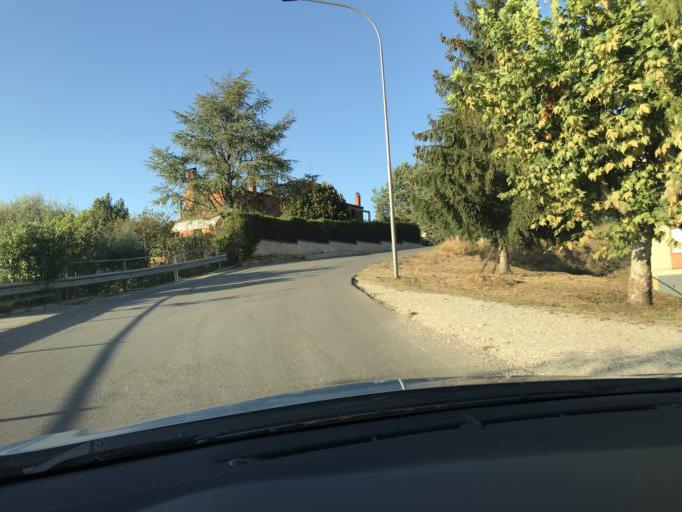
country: IT
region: Umbria
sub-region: Provincia di Terni
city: Amelia
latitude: 42.5492
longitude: 12.4171
